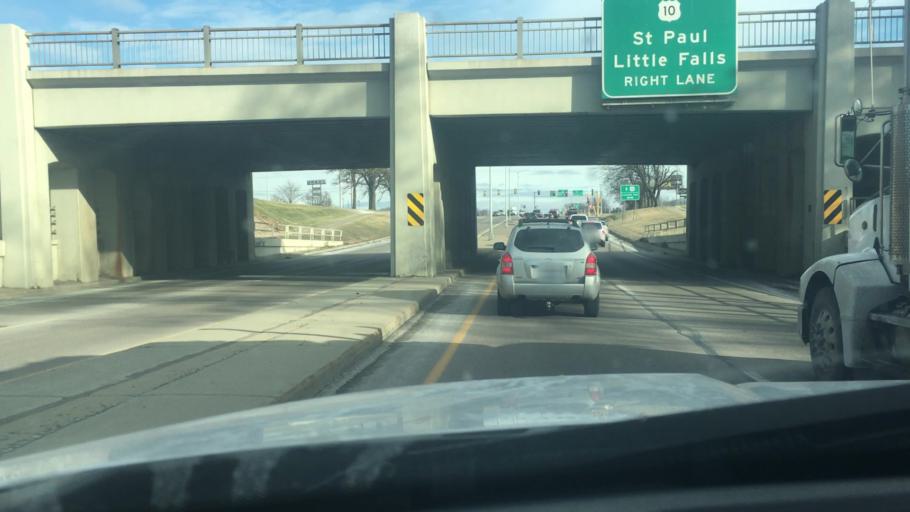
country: US
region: Minnesota
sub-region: Stearns County
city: Saint Cloud
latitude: 45.5636
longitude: -94.1460
